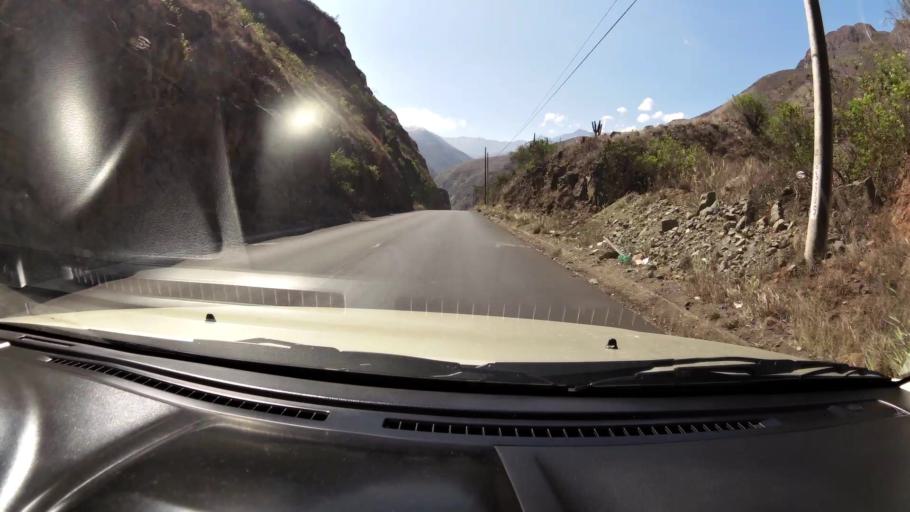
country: EC
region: El Oro
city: Pasaje
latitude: -3.3215
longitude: -79.4719
